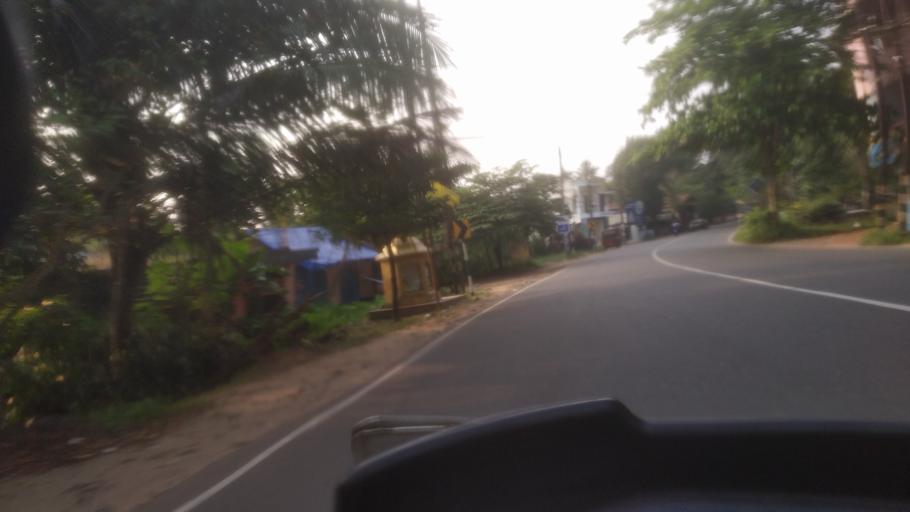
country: IN
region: Kerala
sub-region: Alappuzha
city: Arukutti
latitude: 9.8892
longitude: 76.3731
